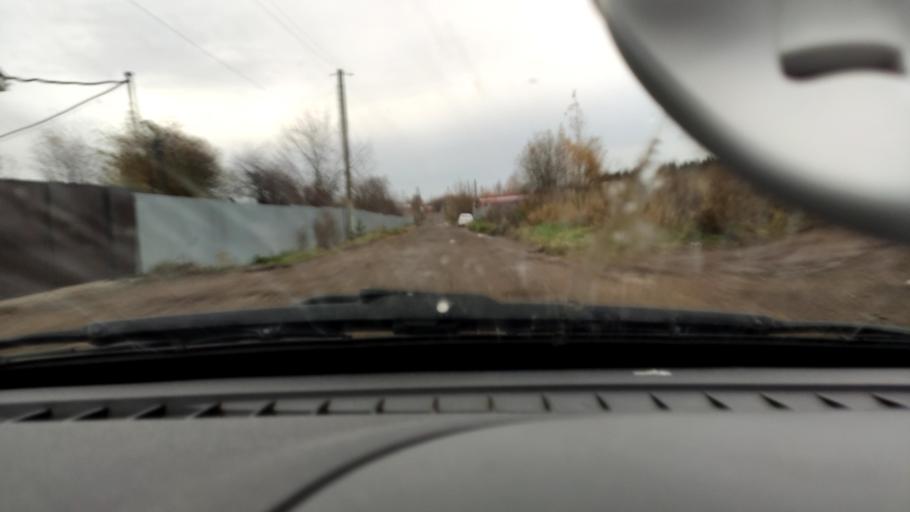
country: RU
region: Perm
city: Kondratovo
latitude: 57.9539
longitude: 56.1671
